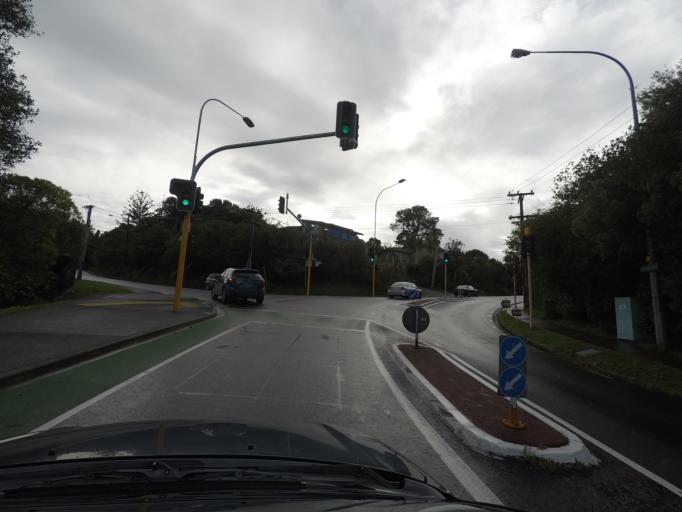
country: NZ
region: Auckland
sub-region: Auckland
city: Rothesay Bay
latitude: -36.7116
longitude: 174.7447
